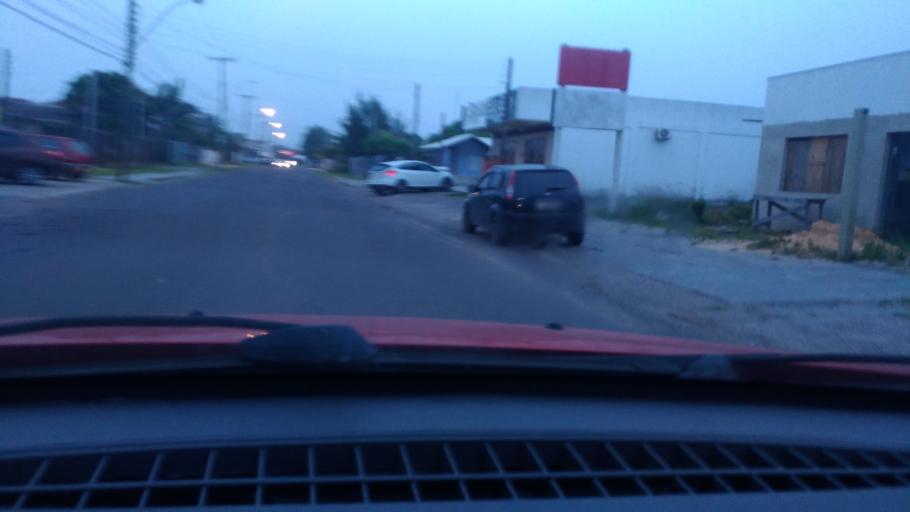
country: BR
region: Rio Grande do Sul
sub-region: Capao Da Canoa
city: Capao da Canoa
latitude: -29.8494
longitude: -50.0640
